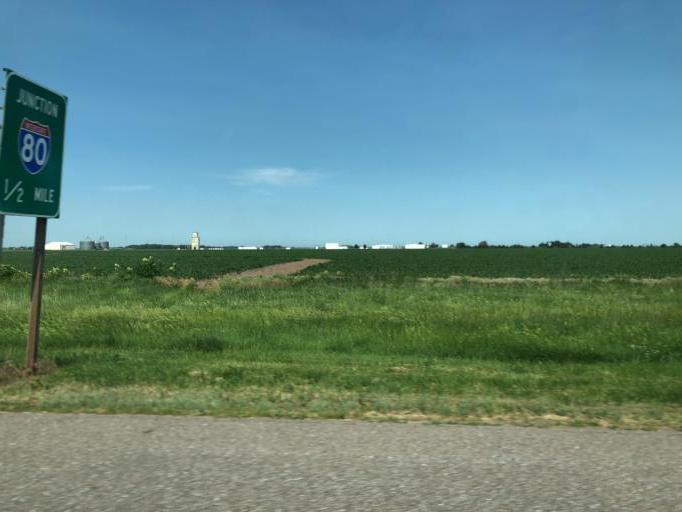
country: US
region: Nebraska
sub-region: York County
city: York
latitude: 40.8115
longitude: -97.5975
